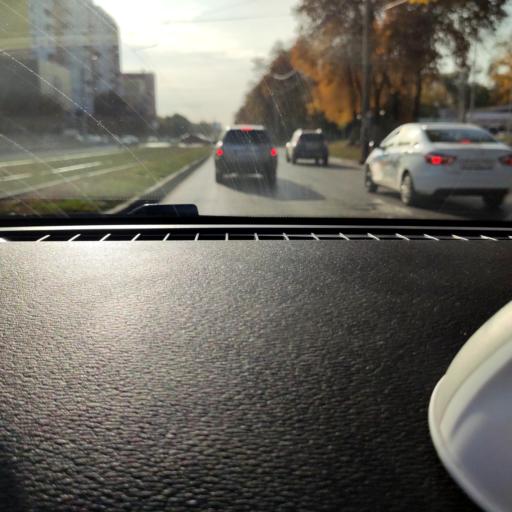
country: RU
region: Samara
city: Samara
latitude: 53.2329
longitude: 50.2232
